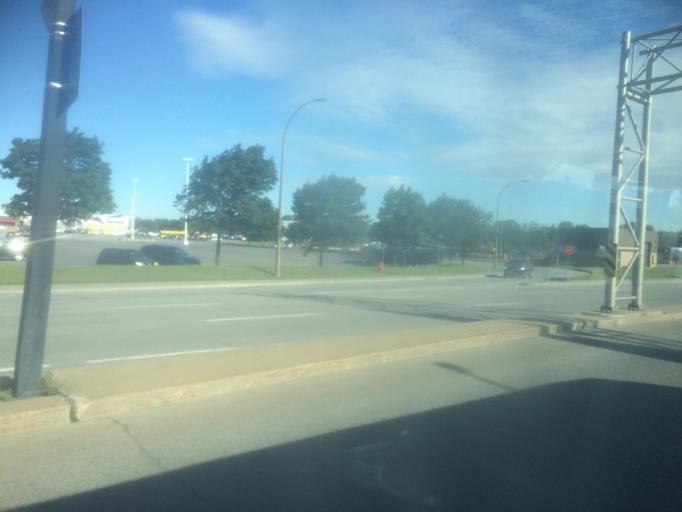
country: CA
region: Quebec
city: Montreal-Est
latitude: 45.5914
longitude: -73.5380
